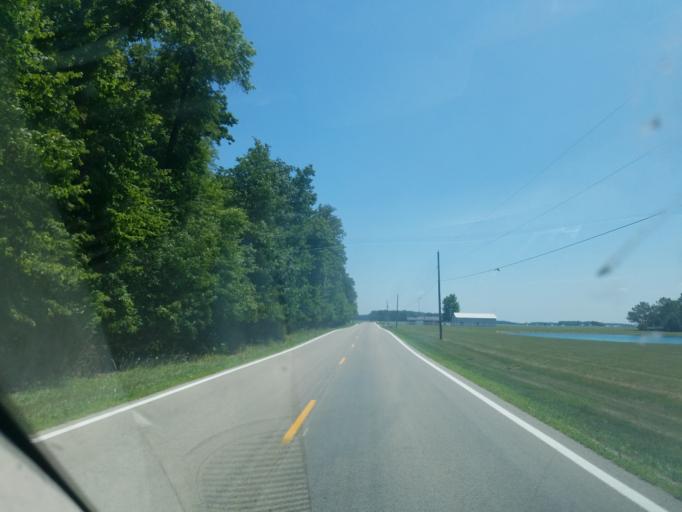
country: US
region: Ohio
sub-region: Allen County
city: Spencerville
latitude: 40.7431
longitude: -84.4089
